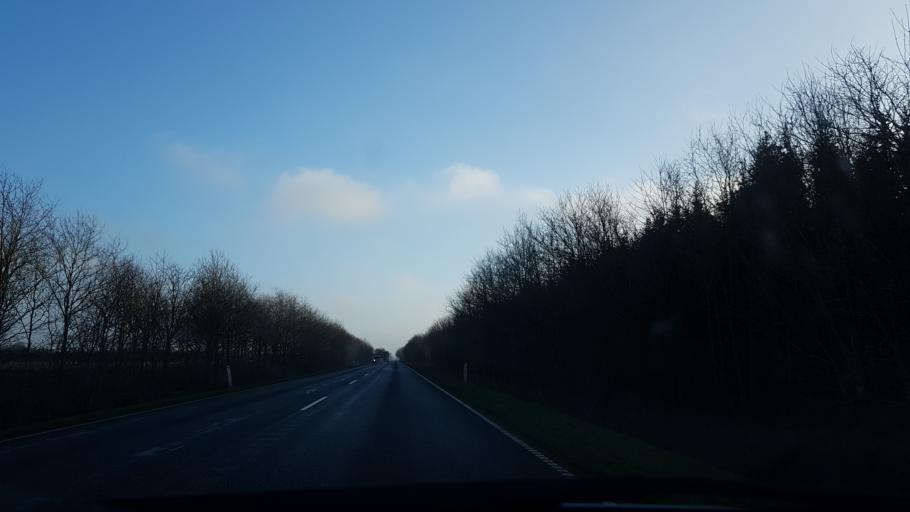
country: DK
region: South Denmark
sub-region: Haderslev Kommune
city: Vojens
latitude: 55.1821
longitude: 9.2319
